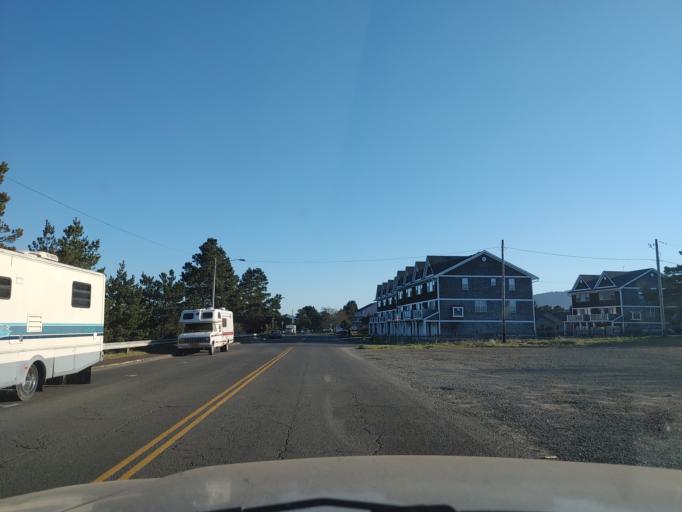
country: US
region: Oregon
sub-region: Clatsop County
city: Seaside
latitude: 46.0007
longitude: -123.9231
